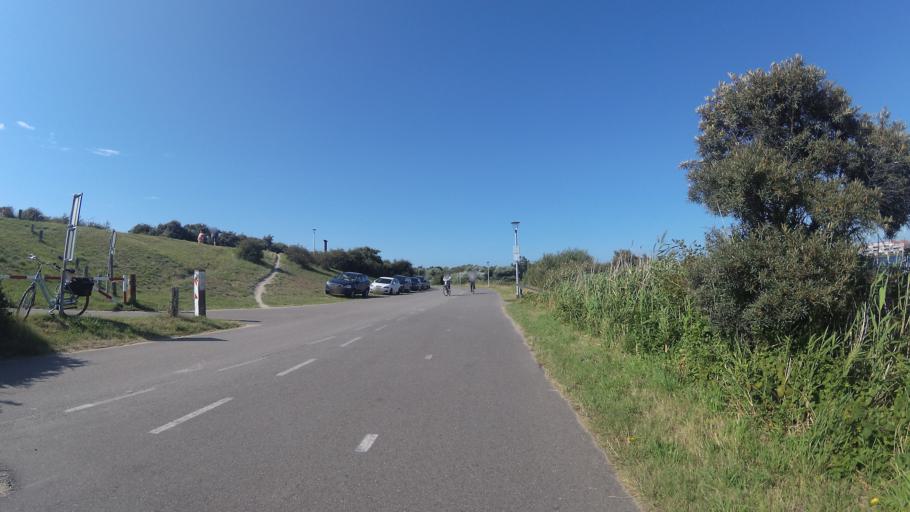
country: NL
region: Zeeland
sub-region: Gemeente Vlissingen
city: Vlissingen
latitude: 51.5237
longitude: 3.4422
